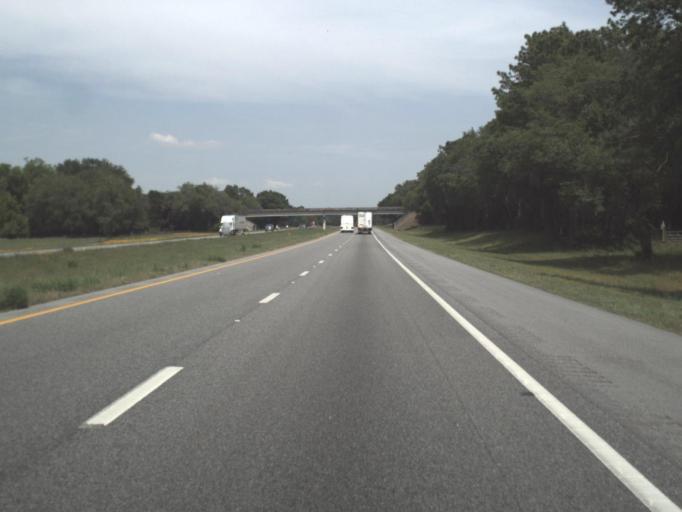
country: US
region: Florida
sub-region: Suwannee County
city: Live Oak
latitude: 30.3490
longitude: -83.0683
